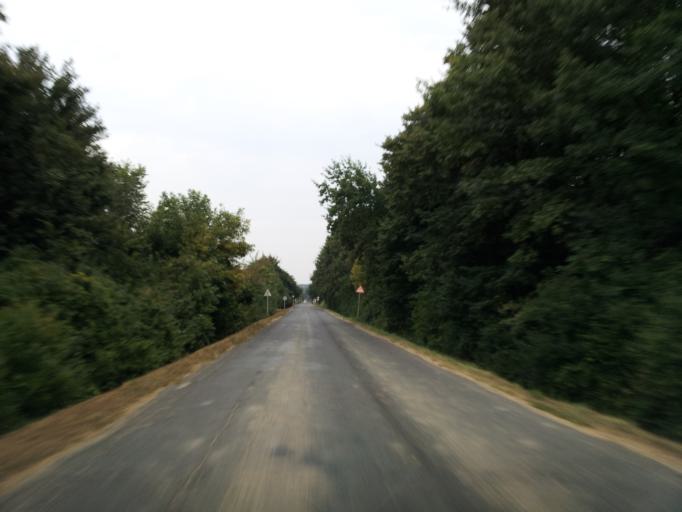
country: HU
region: Vas
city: Sarvar
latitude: 47.2052
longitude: 16.9222
